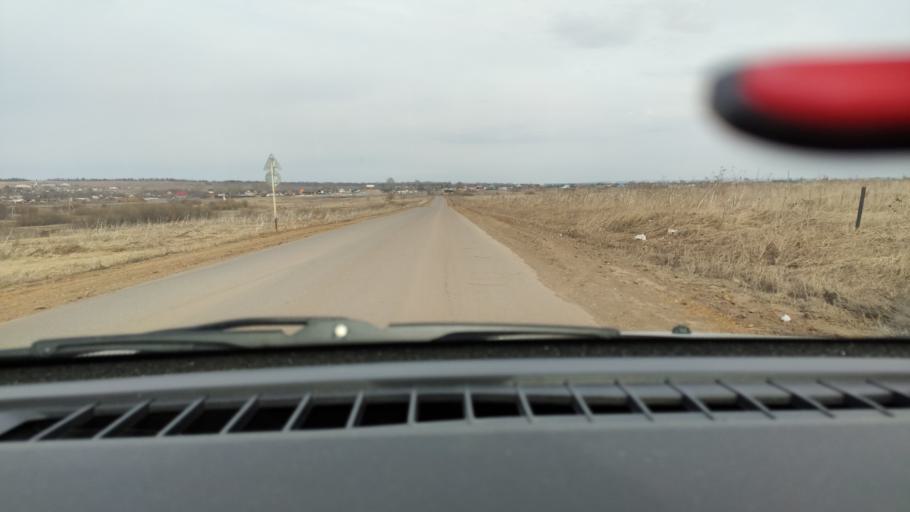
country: RU
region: Perm
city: Kultayevo
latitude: 57.9001
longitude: 55.9933
